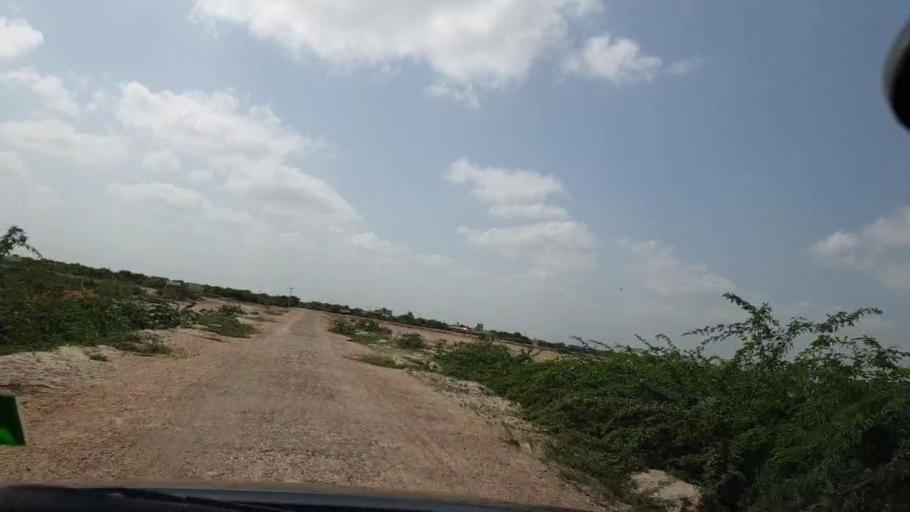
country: PK
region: Sindh
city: Kadhan
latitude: 24.5897
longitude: 69.1593
